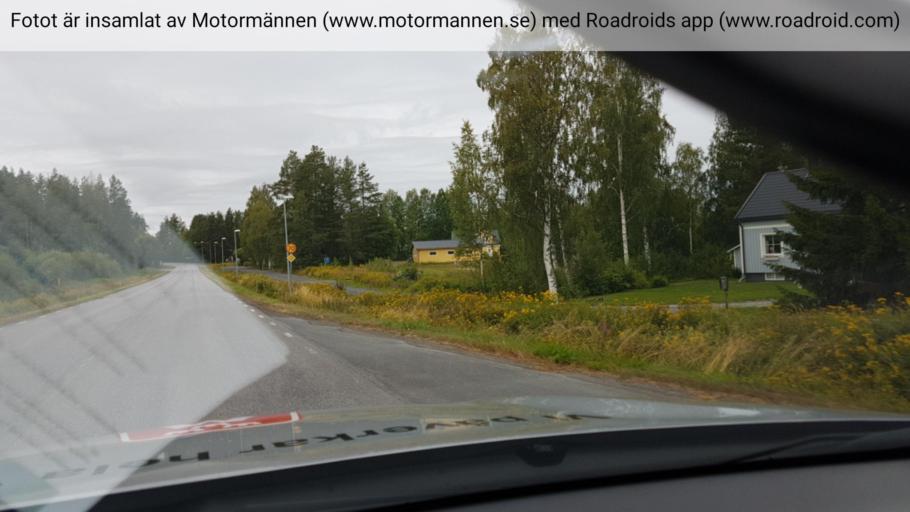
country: SE
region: Norrbotten
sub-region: Bodens Kommun
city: Boden
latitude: 65.8147
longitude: 21.6208
